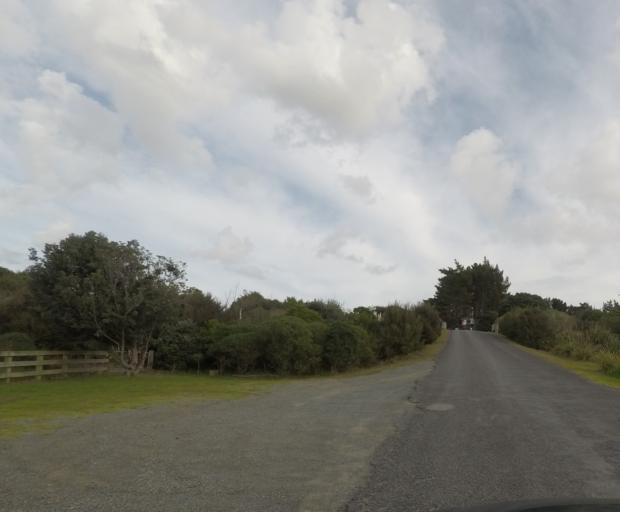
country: NZ
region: Northland
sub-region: Whangarei
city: Ruakaka
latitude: -35.9352
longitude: 174.4568
